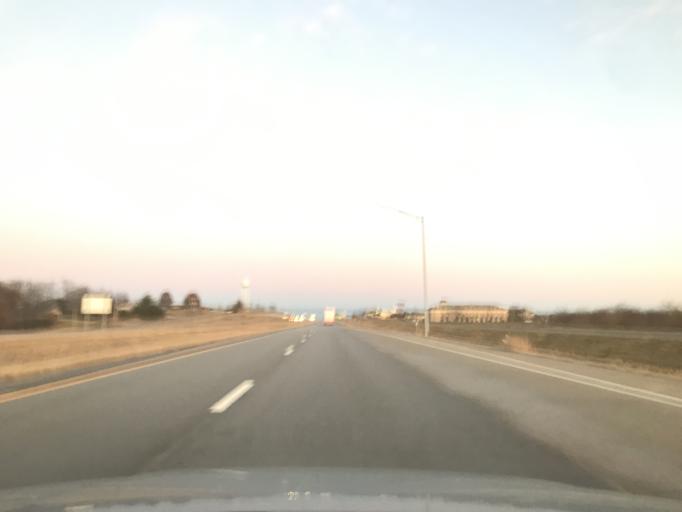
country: US
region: Missouri
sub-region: Marion County
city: Hannibal
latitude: 39.7135
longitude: -91.4406
